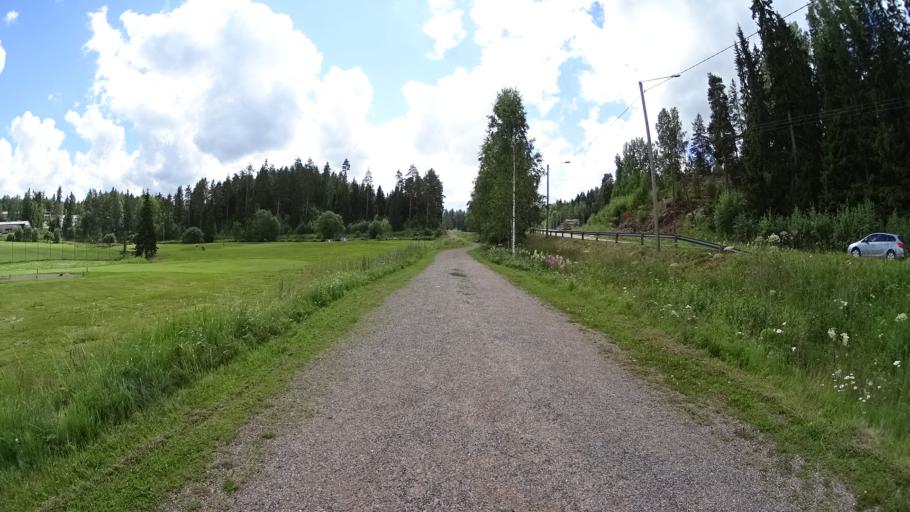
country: FI
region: Uusimaa
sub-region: Helsinki
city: Espoo
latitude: 60.3555
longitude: 24.6462
